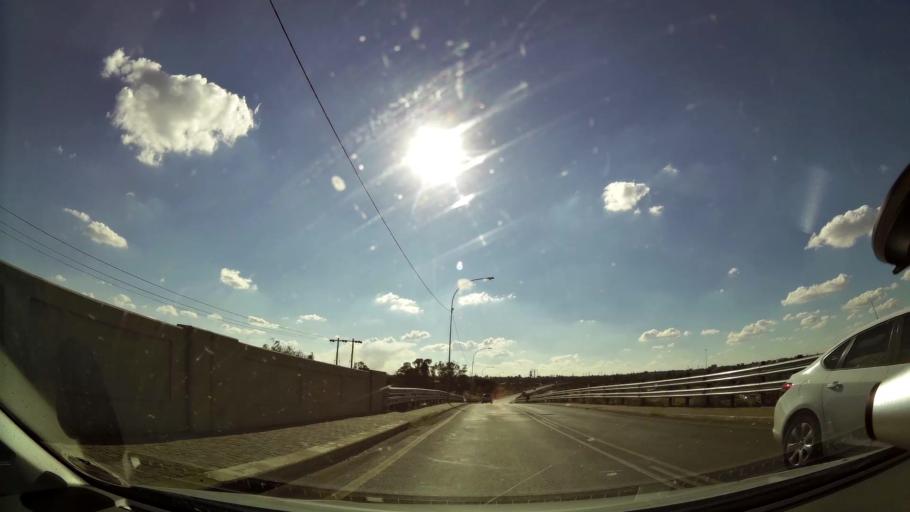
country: ZA
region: Northern Cape
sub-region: Frances Baard District Municipality
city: Kimberley
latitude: -28.7786
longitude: 24.7663
